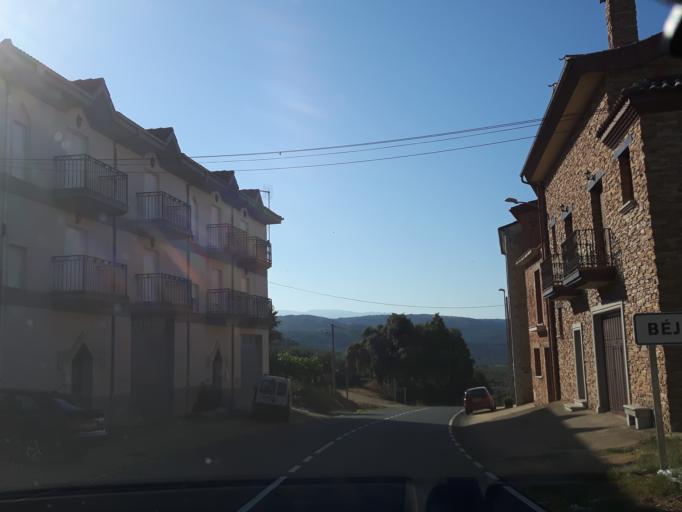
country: ES
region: Castille and Leon
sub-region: Provincia de Salamanca
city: Sotoserrano
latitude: 40.4344
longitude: -6.0307
